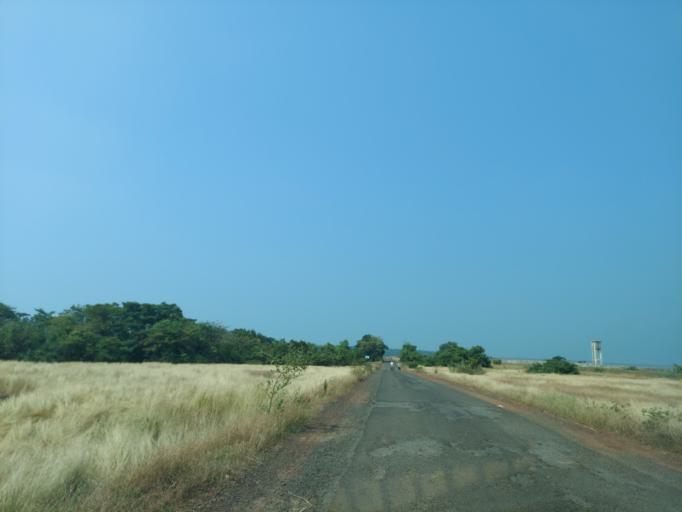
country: IN
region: Maharashtra
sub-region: Sindhudurg
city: Malvan
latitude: 15.9978
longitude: 73.5161
